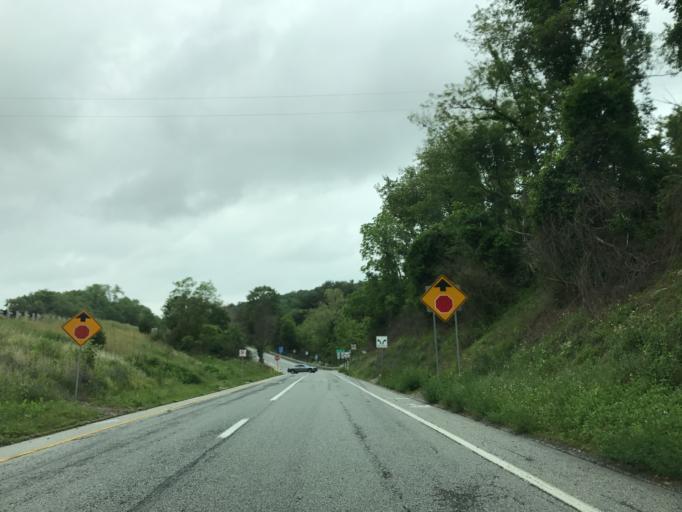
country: US
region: Pennsylvania
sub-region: York County
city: Loganville
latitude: 39.8260
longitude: -76.6840
